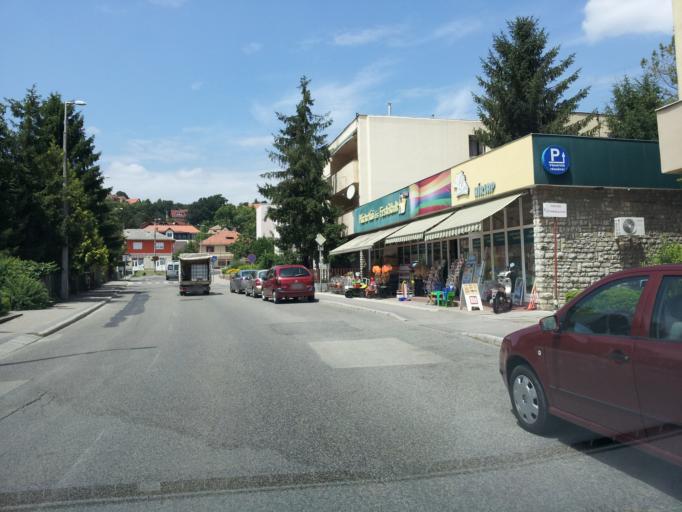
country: HU
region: Veszprem
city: Balatonalmadi
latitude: 47.0313
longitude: 18.0135
